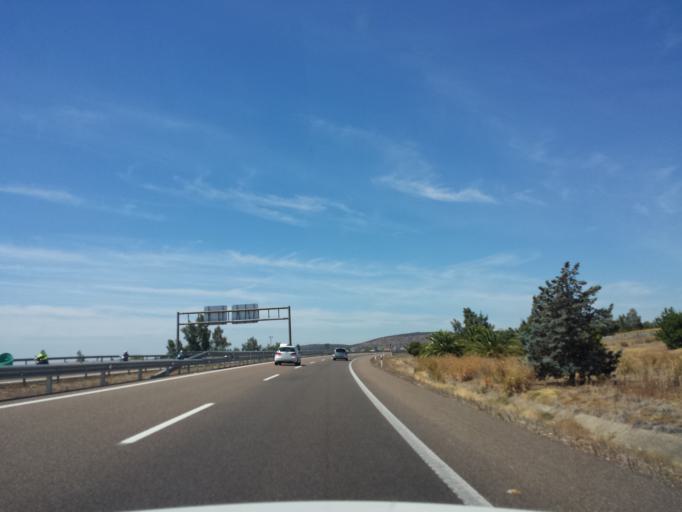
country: ES
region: Extremadura
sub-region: Provincia de Badajoz
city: Valdetorres
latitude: 38.9923
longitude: -6.1006
